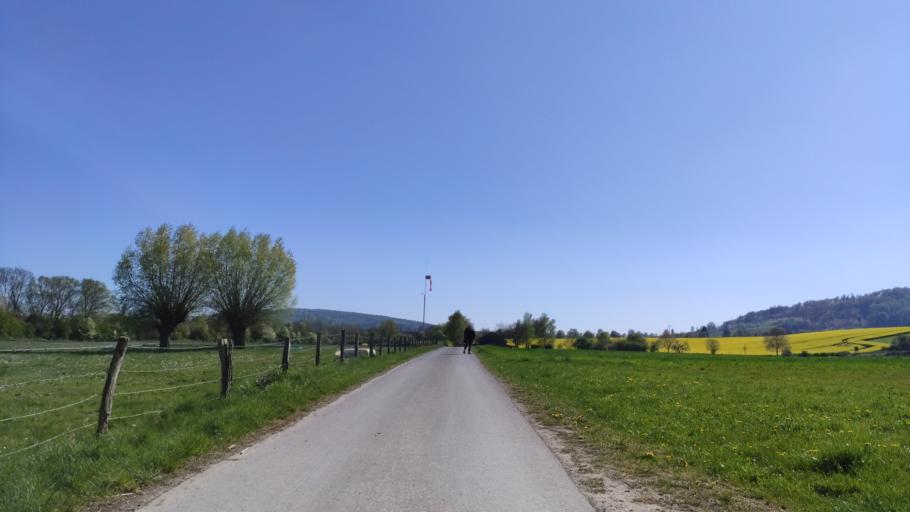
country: DE
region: Lower Saxony
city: Boffzen
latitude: 51.7453
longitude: 9.3612
